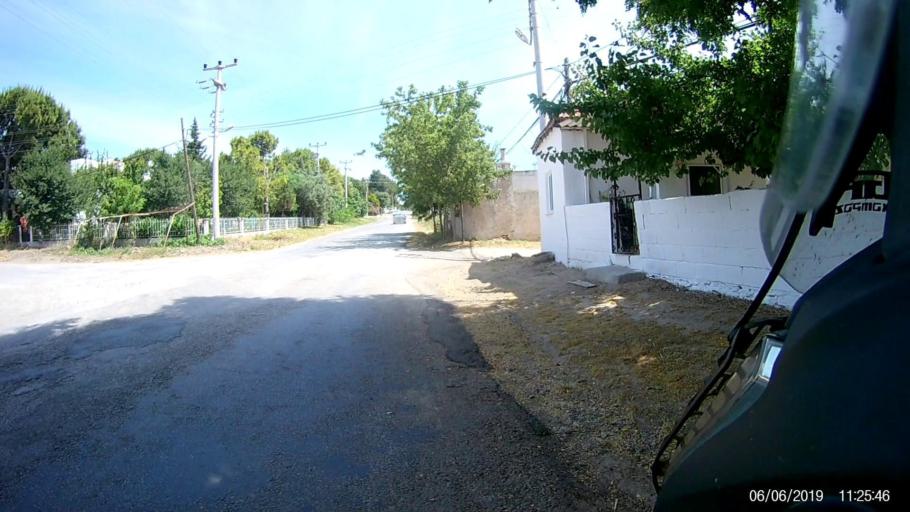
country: TR
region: Canakkale
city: Gulpinar
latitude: 39.6299
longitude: 26.1833
